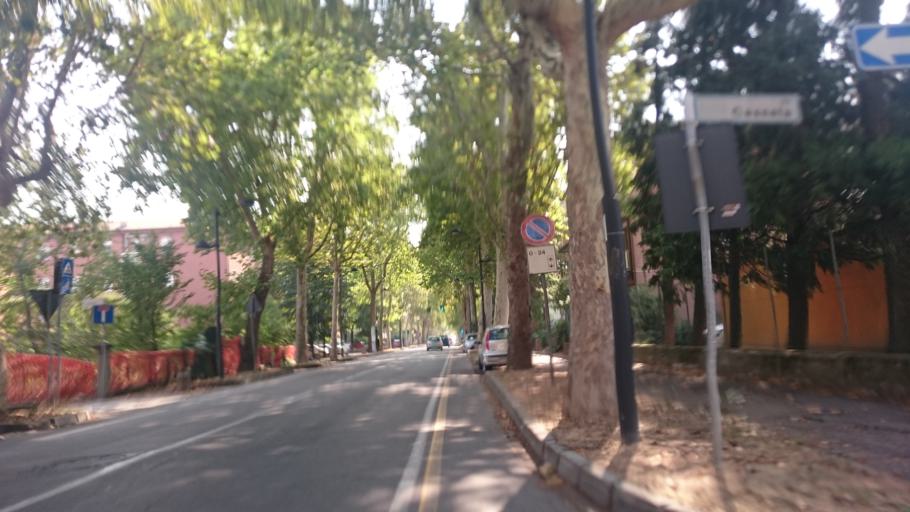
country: IT
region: Emilia-Romagna
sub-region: Provincia di Reggio Emilia
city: Reggio nell'Emilia
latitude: 44.7048
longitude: 10.6489
